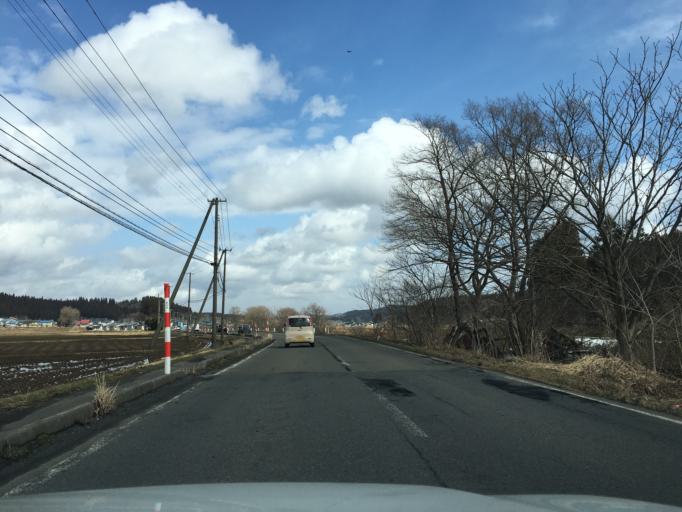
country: JP
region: Akita
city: Takanosu
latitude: 40.0385
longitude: 140.2785
